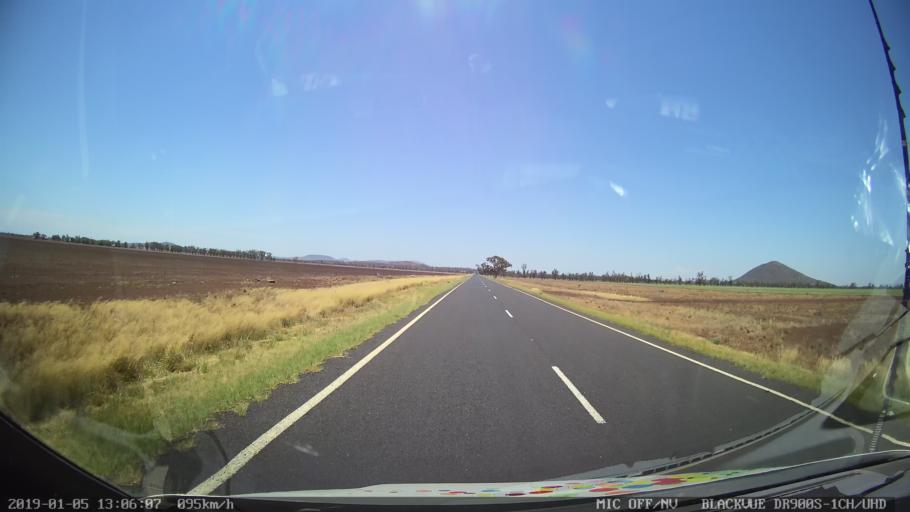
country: AU
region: New South Wales
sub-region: Gunnedah
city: Gunnedah
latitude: -31.0951
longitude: 149.8641
